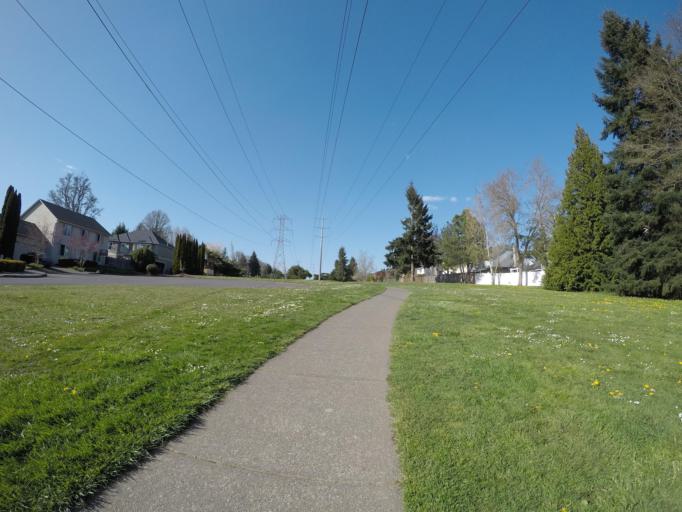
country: US
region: Oregon
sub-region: Washington County
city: Oak Hills
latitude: 45.5437
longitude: -122.8464
